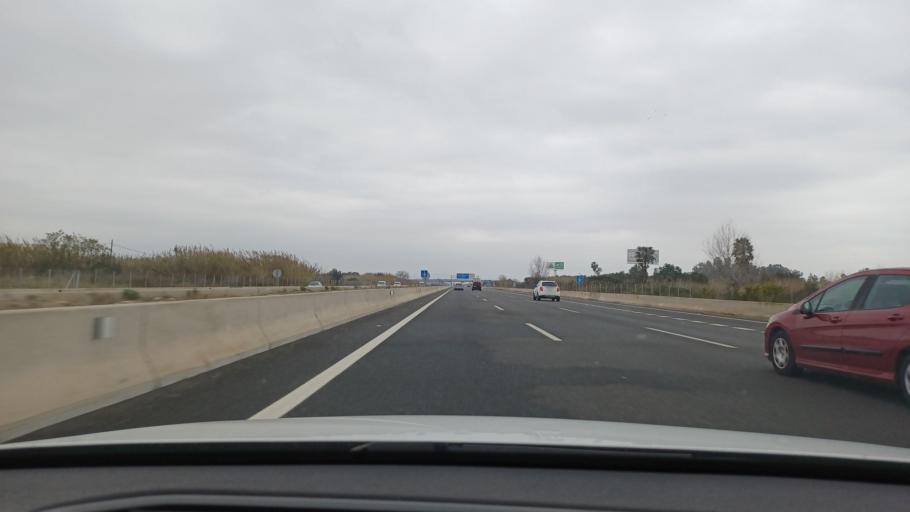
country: ES
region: Valencia
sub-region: Provincia de Valencia
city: Albuixech
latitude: 39.5625
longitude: -0.2965
